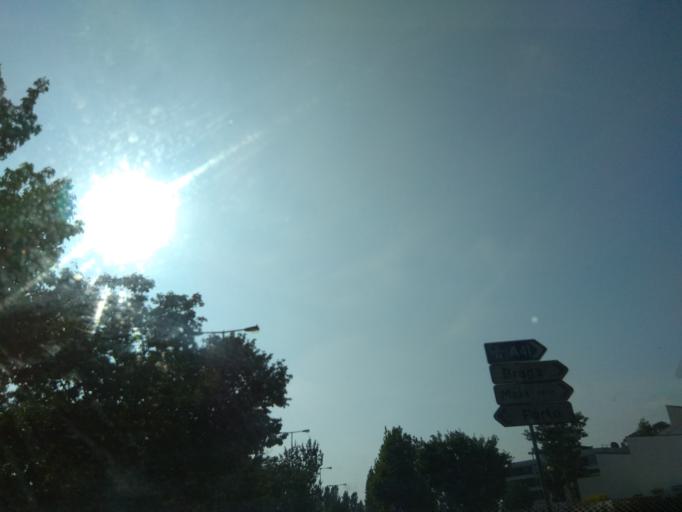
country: PT
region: Porto
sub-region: Maia
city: Maia
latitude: 41.2265
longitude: -8.6241
